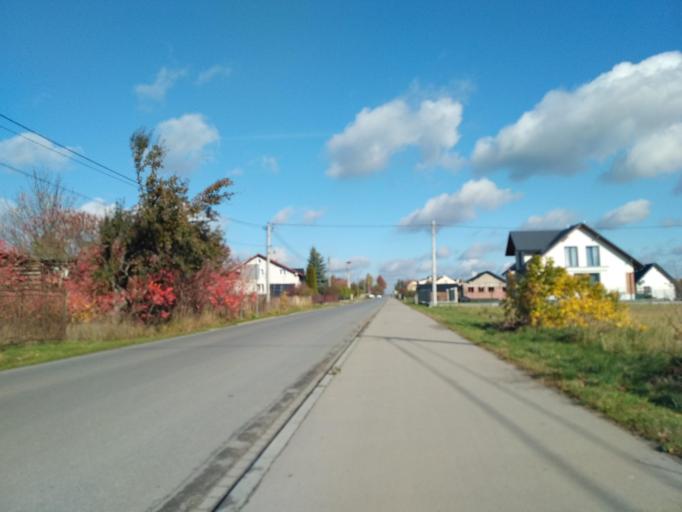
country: PL
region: Subcarpathian Voivodeship
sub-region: Powiat rzeszowski
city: Trzciana
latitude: 50.1003
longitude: 21.8521
